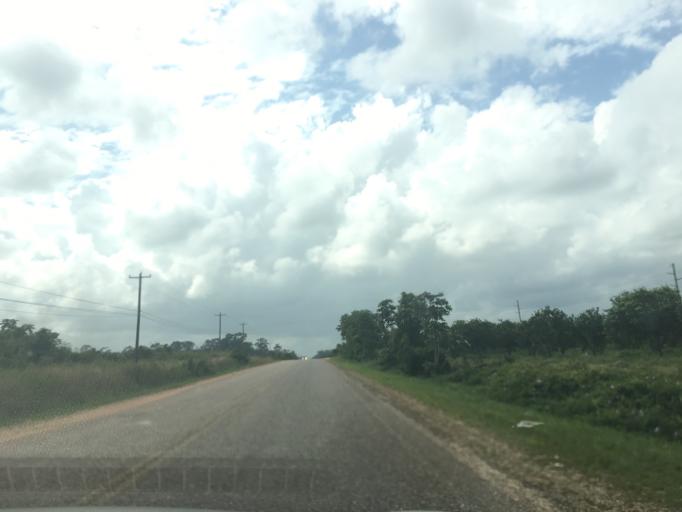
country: BZ
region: Stann Creek
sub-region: Dangriga
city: Dangriga
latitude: 16.9717
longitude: -88.3027
